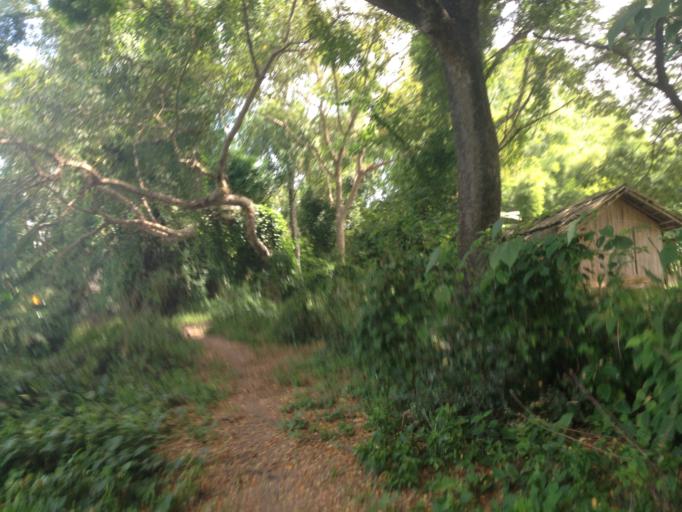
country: TH
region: Chiang Mai
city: Hang Dong
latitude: 18.7038
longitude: 98.9191
